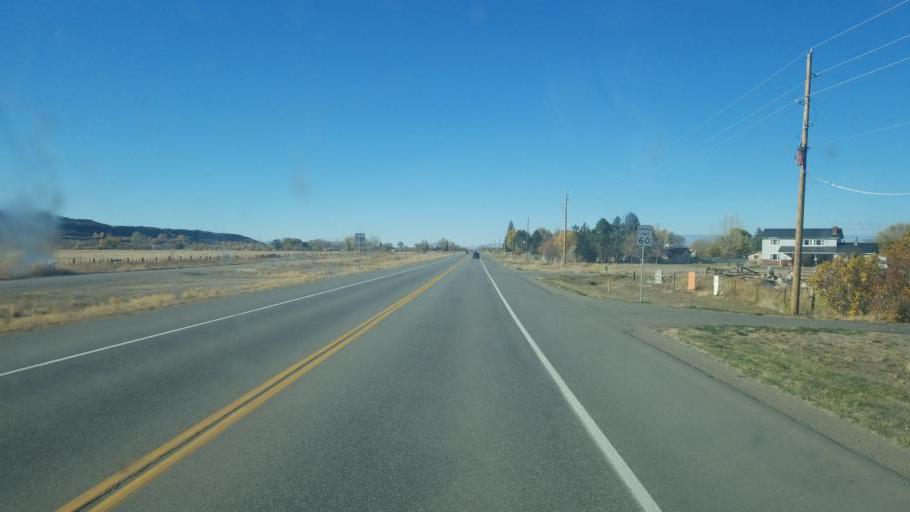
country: US
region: Colorado
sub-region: Montrose County
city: Montrose
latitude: 38.3823
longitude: -107.8224
